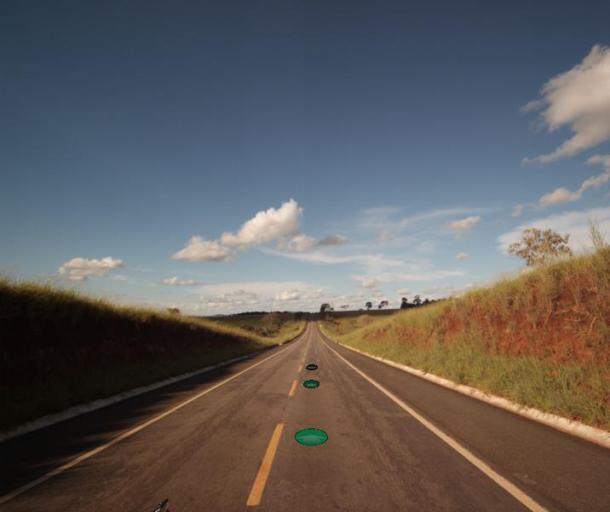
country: BR
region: Goias
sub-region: Itaberai
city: Itaberai
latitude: -15.9709
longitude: -49.6727
